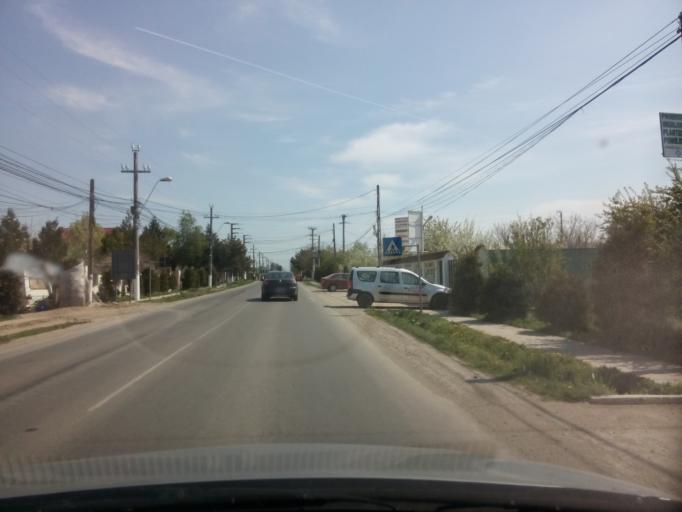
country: RO
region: Ilfov
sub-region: Comuna Corbeanca
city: Tamasi
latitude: 44.5915
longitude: 26.0271
